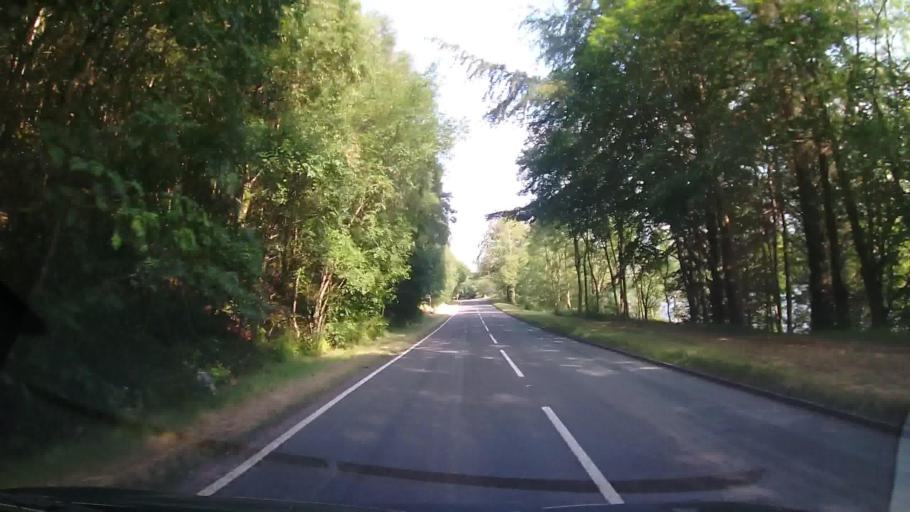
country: GB
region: Wales
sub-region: Gwynedd
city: Bala
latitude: 52.9540
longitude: -3.6926
